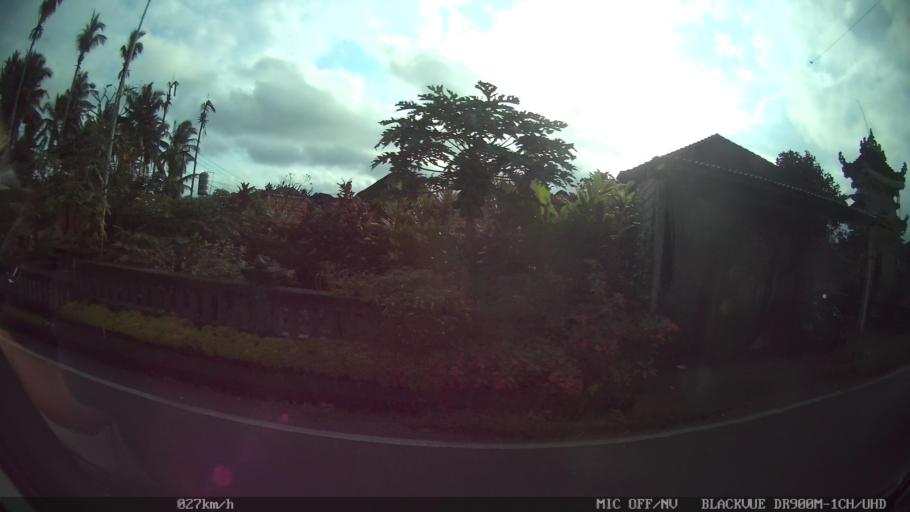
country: ID
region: Bali
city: Banjar Tebongkang
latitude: -8.5209
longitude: 115.2505
